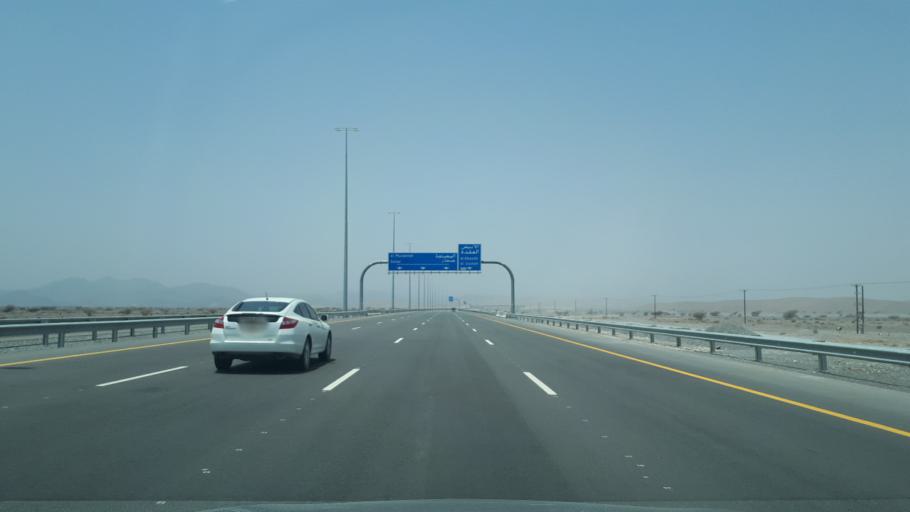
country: OM
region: Al Batinah
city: Barka'
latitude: 23.5387
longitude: 57.6754
